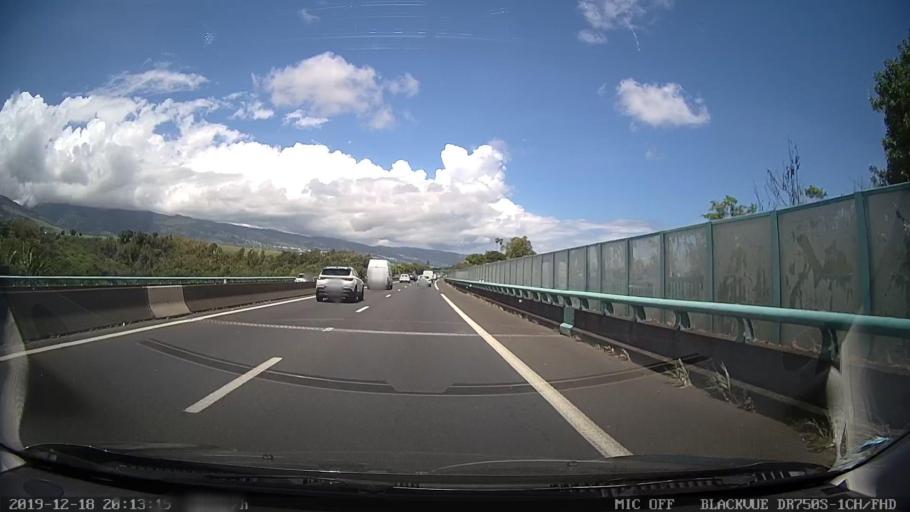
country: RE
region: Reunion
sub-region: Reunion
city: Sainte-Marie
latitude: -20.9025
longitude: 55.5531
